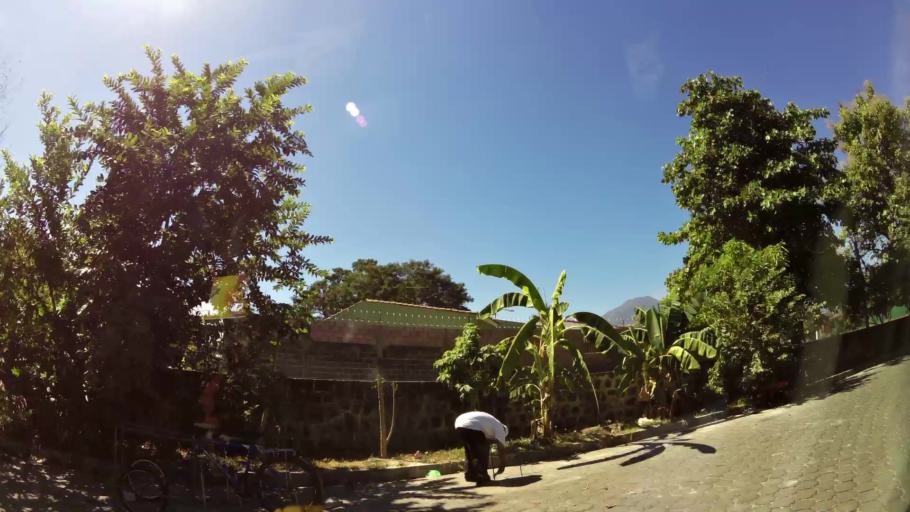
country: SV
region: San Miguel
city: San Miguel
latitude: 13.4804
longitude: -88.1704
